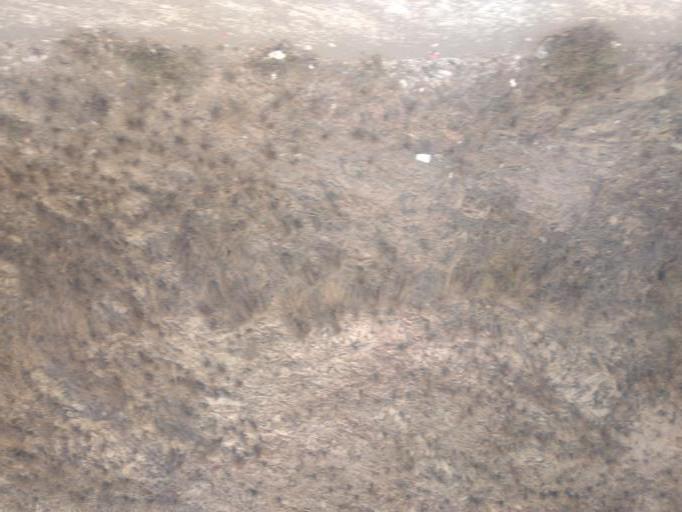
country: MX
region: Colima
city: El Colomo
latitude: 19.0605
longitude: -104.2696
